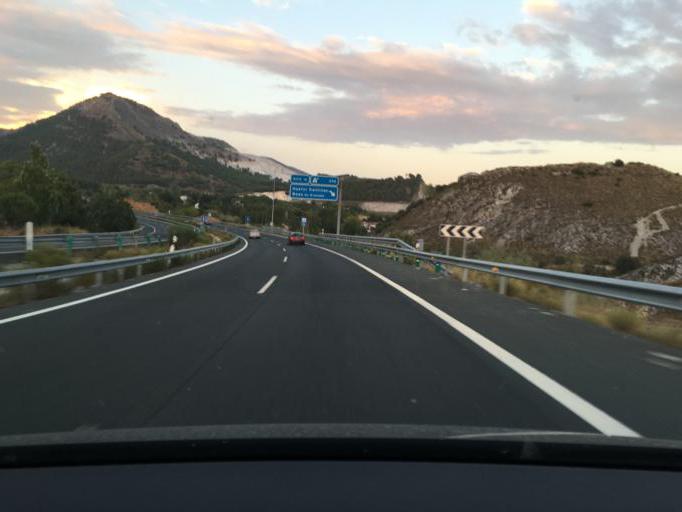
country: ES
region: Andalusia
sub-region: Provincia de Granada
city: Huetor Santillan
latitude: 37.2276
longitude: -3.5052
